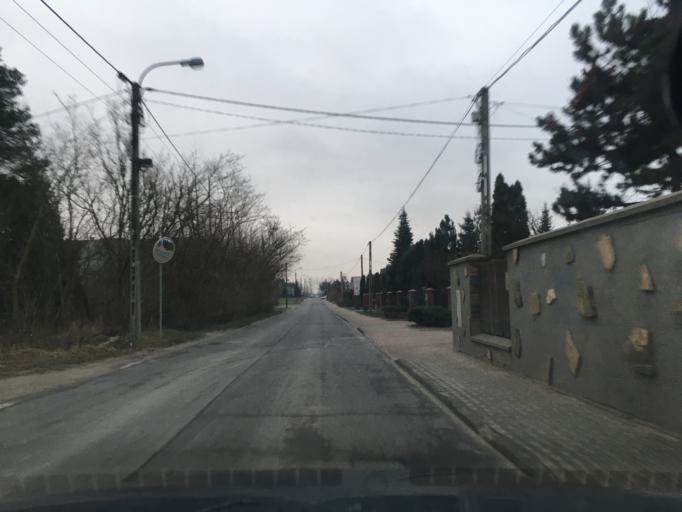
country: PL
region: Masovian Voivodeship
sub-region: Powiat piaseczynski
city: Mysiadlo
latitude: 52.1199
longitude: 20.9794
